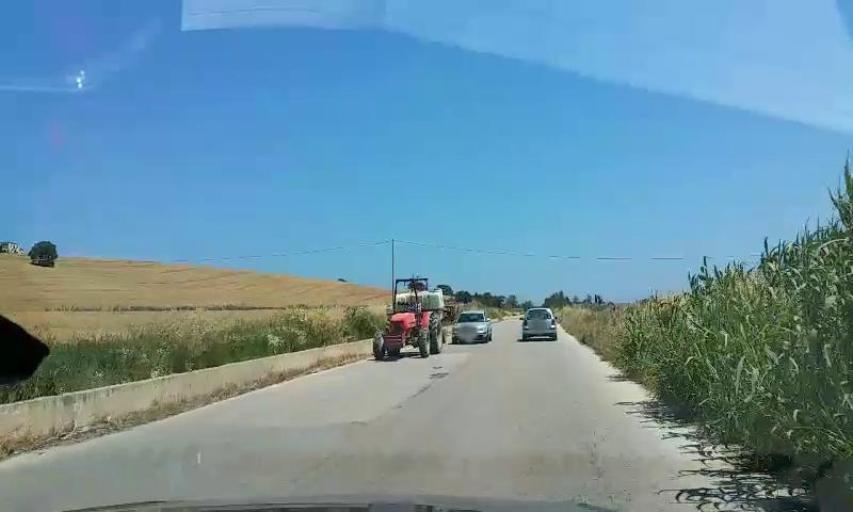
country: IT
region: Molise
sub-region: Provincia di Campobasso
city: Termoli
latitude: 41.9998
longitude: 14.9567
